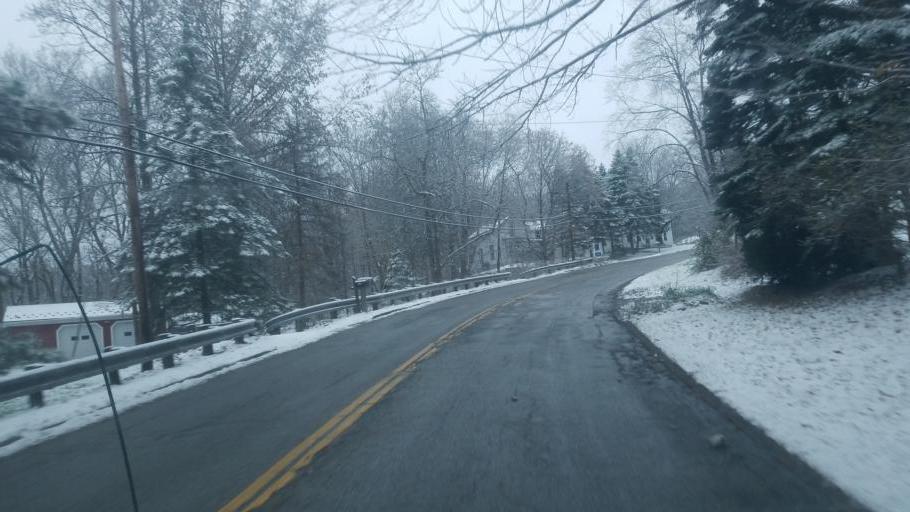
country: US
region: Ohio
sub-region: Geauga County
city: Burton
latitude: 41.4646
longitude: -81.1443
